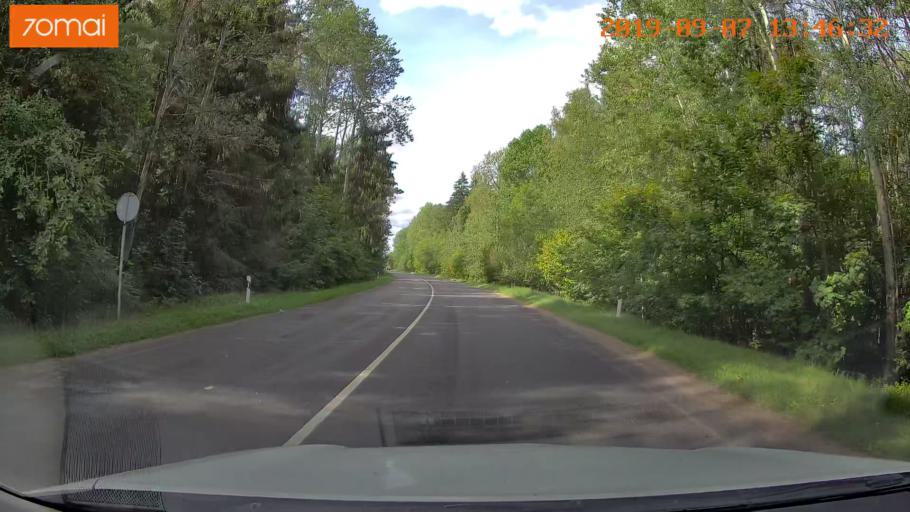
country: LT
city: Baltoji Voke
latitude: 54.5916
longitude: 25.2313
